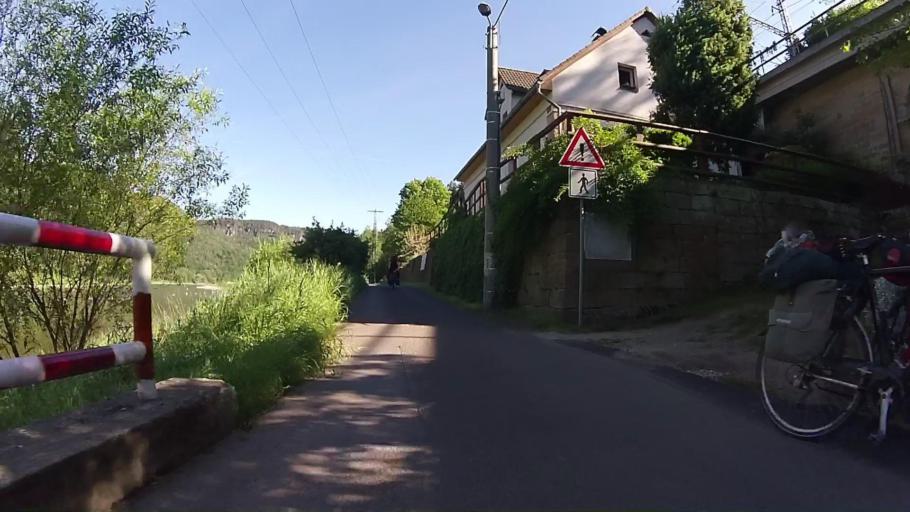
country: CZ
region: Ustecky
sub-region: Okres Decin
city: Decin
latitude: 50.8426
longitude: 14.2174
